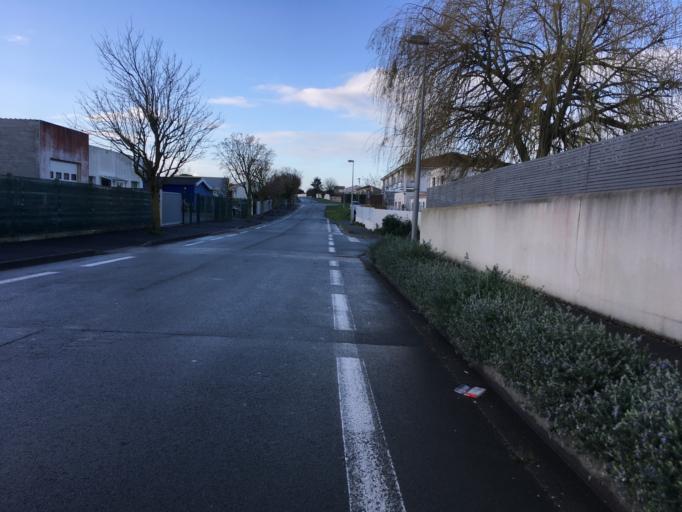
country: FR
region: Poitou-Charentes
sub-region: Departement de la Charente-Maritime
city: Nieul-sur-Mer
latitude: 46.2023
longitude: -1.1719
